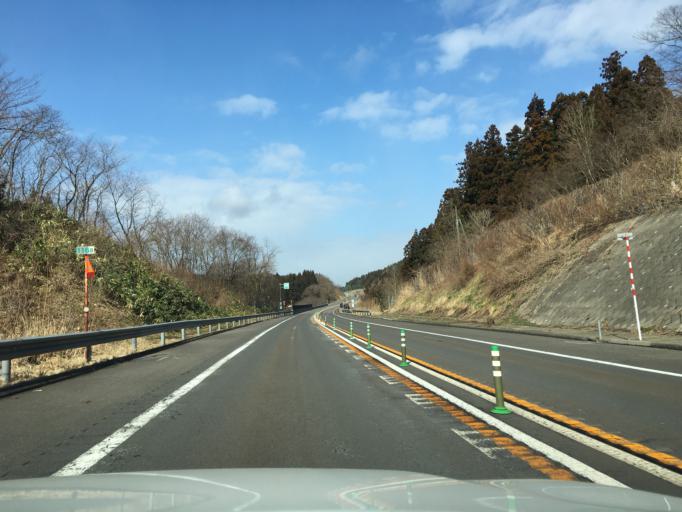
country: JP
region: Akita
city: Akita
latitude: 39.7435
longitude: 140.1618
